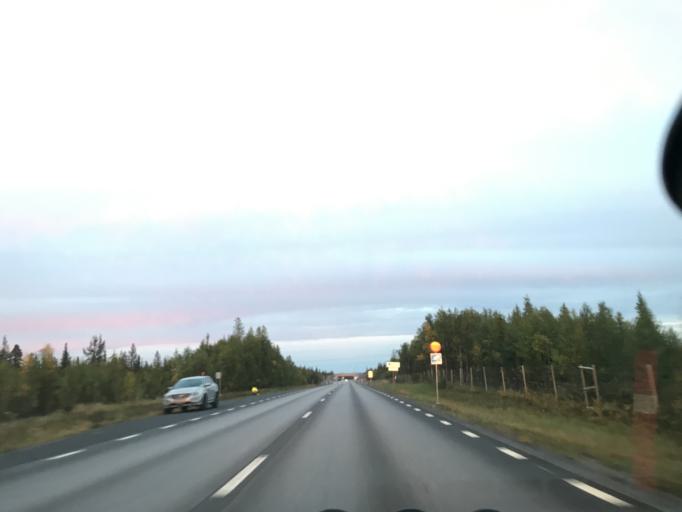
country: SE
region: Norrbotten
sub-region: Gallivare Kommun
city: Malmberget
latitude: 67.6962
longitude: 20.7968
